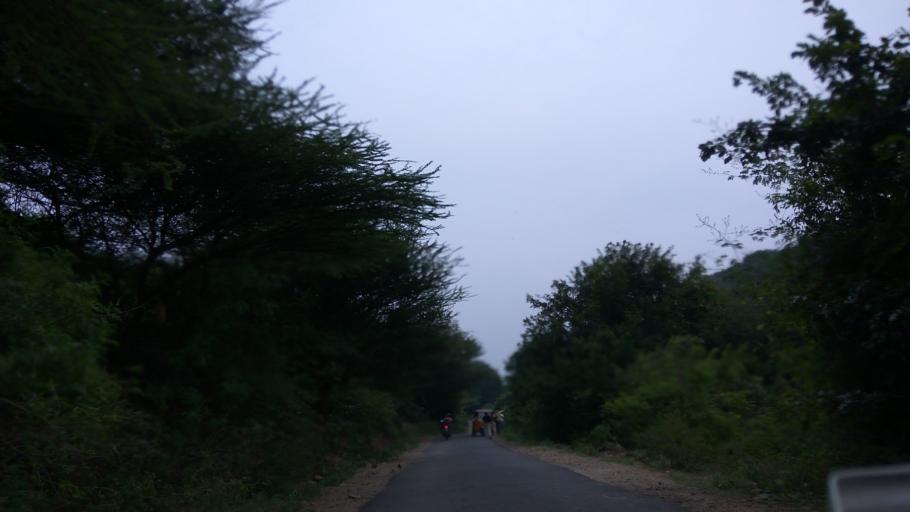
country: IN
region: Tamil Nadu
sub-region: Dharmapuri
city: Dharmapuri
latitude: 12.0110
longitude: 78.1324
